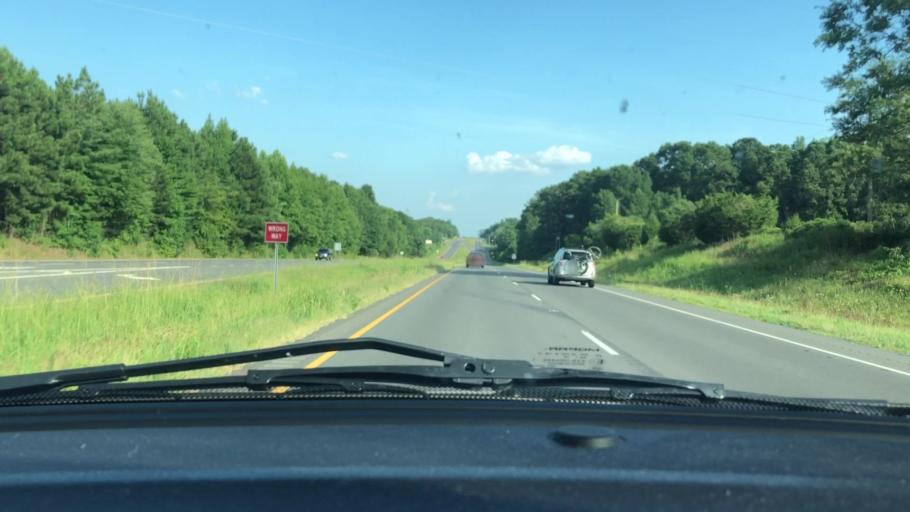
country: US
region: North Carolina
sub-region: Chatham County
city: Siler City
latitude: 35.6371
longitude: -79.3743
